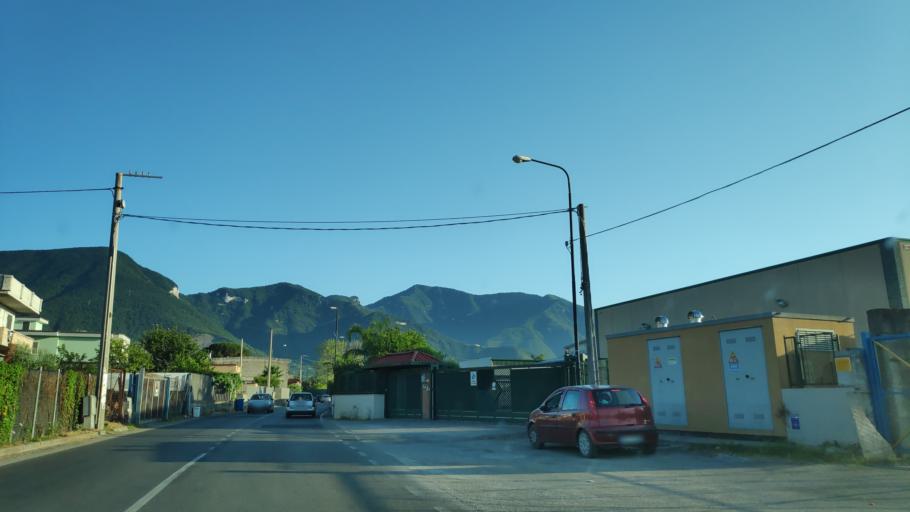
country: IT
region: Campania
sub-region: Provincia di Salerno
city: Pagani
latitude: 40.7590
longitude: 14.6155
